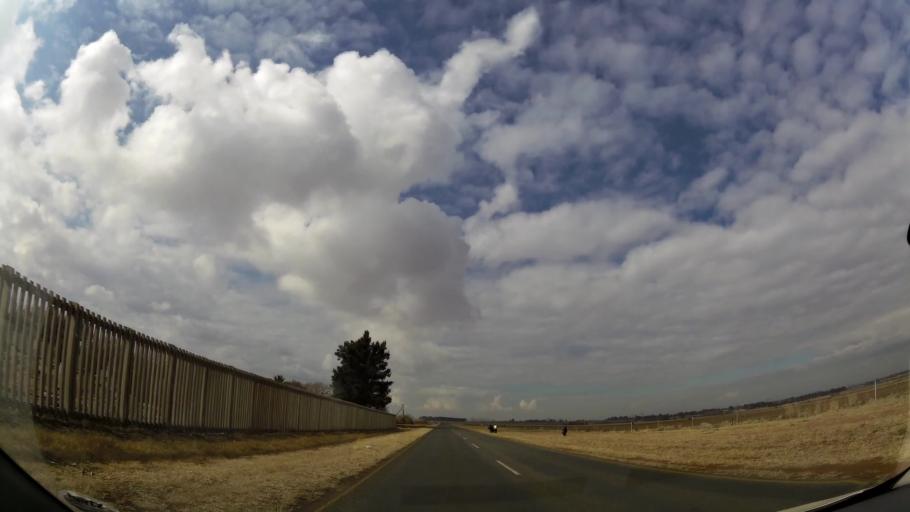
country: ZA
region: Gauteng
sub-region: Sedibeng District Municipality
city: Meyerton
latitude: -26.6145
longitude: 28.0519
